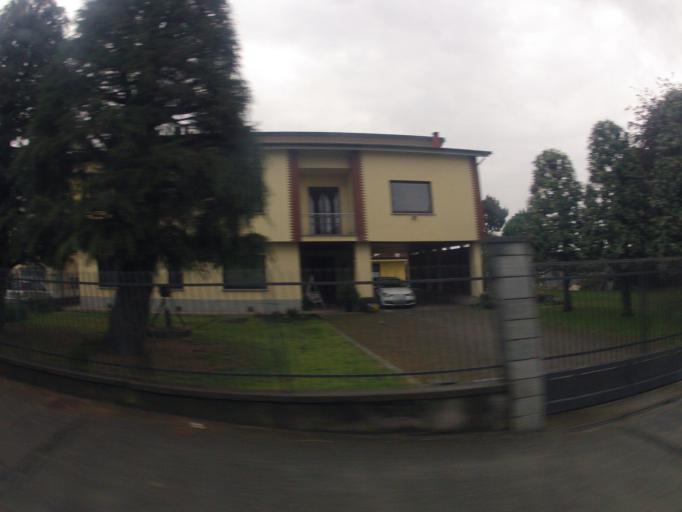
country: IT
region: Piedmont
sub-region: Provincia di Cuneo
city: Moretta
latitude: 44.7646
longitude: 7.5430
